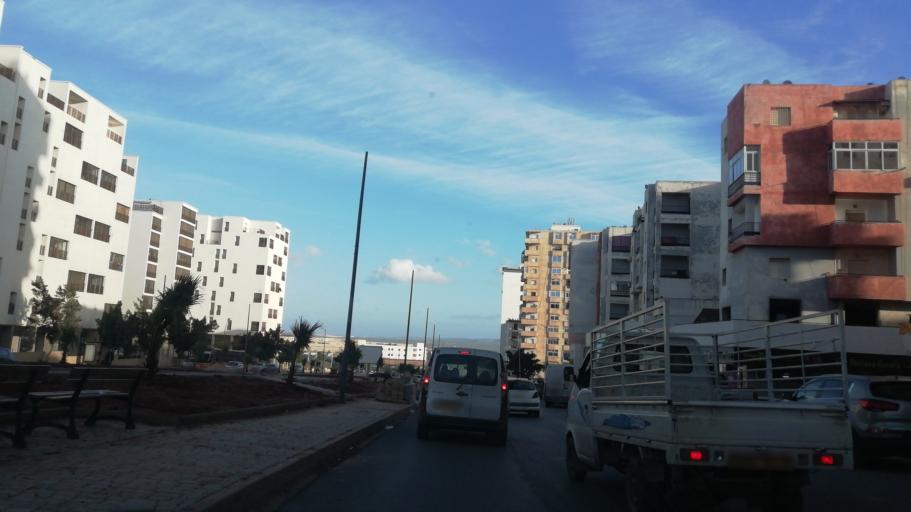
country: DZ
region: Oran
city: Bir el Djir
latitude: 35.7058
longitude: -0.5572
